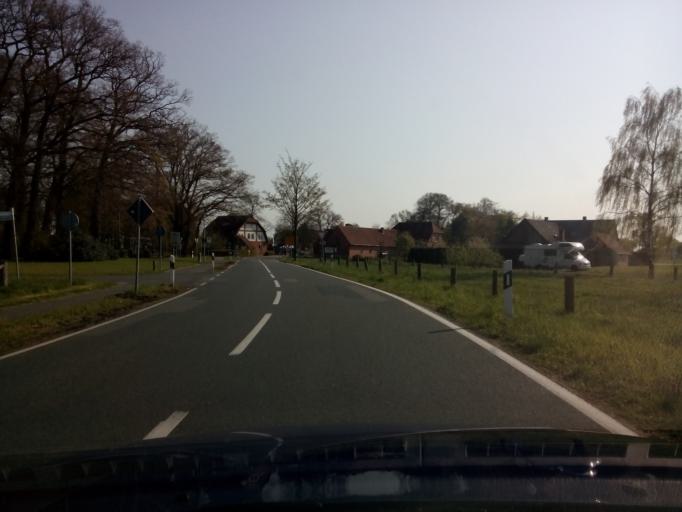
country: DE
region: Lower Saxony
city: Bruchhausen-Vilsen
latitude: 52.8037
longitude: 8.9742
